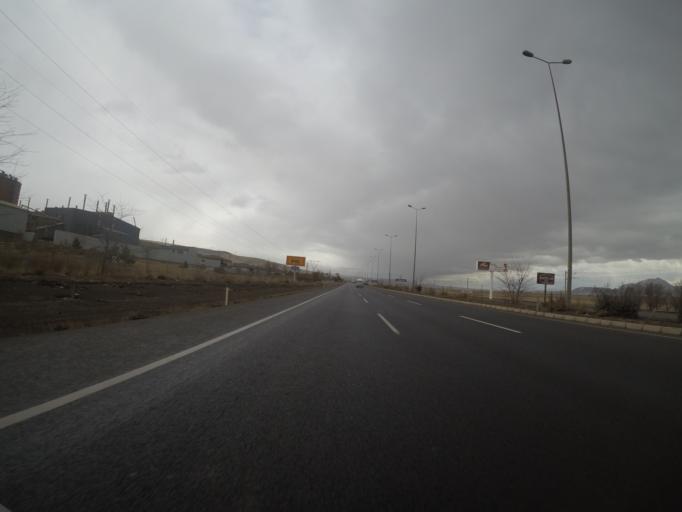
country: TR
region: Kayseri
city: Incesu
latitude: 38.7125
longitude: 35.2641
